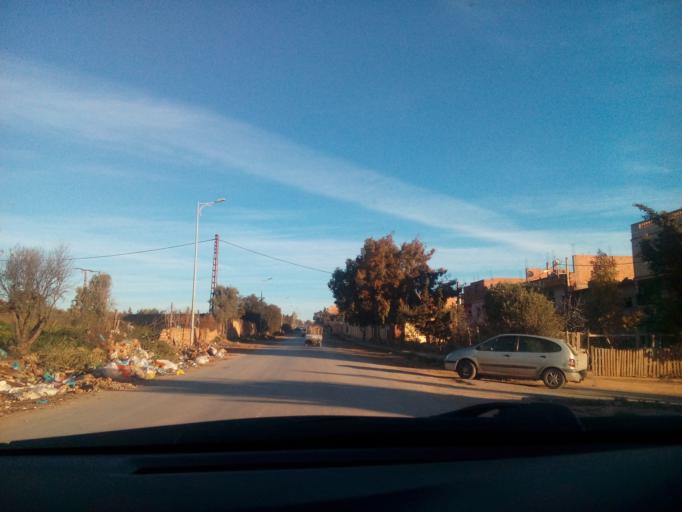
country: DZ
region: Oran
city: Es Senia
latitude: 35.6302
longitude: -0.6742
